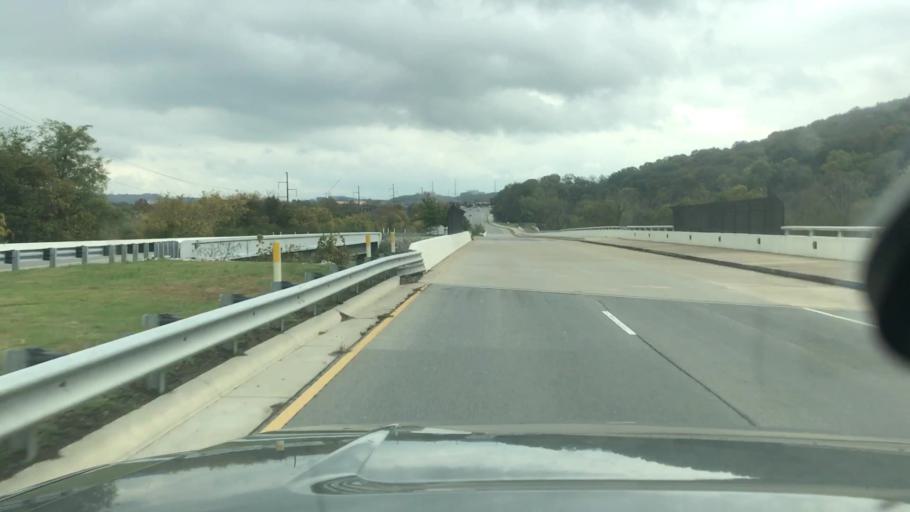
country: US
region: Tennessee
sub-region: Williamson County
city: Franklin
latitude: 35.9450
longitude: -86.8477
